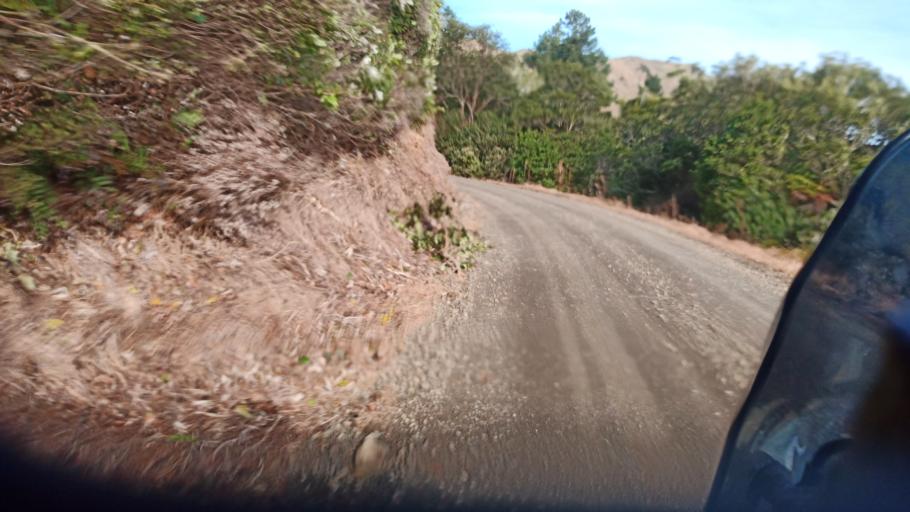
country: NZ
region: Gisborne
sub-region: Gisborne District
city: Gisborne
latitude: -38.4568
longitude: 177.5383
